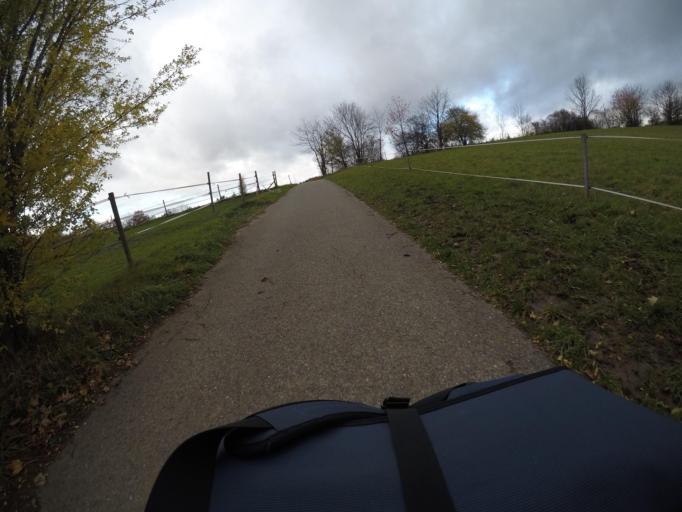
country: DE
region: Baden-Wuerttemberg
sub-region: Tuebingen Region
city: Gomaringen
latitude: 48.4475
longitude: 9.1481
